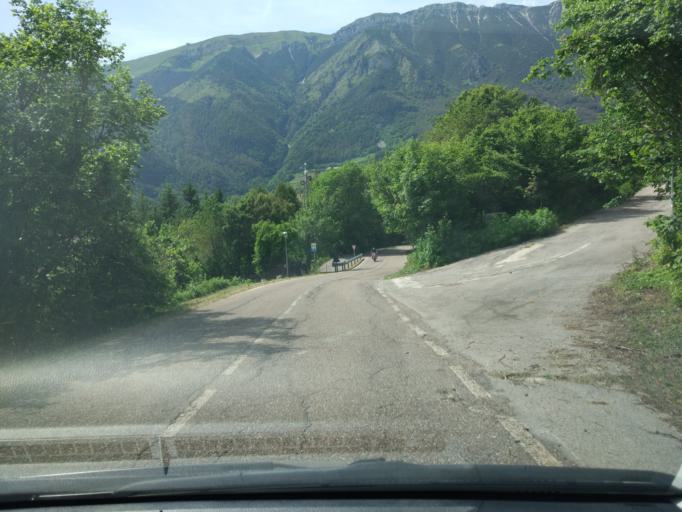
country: IT
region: Veneto
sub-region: Provincia di Verona
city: Ferrara di Monte Baldo
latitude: 45.6733
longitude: 10.8629
